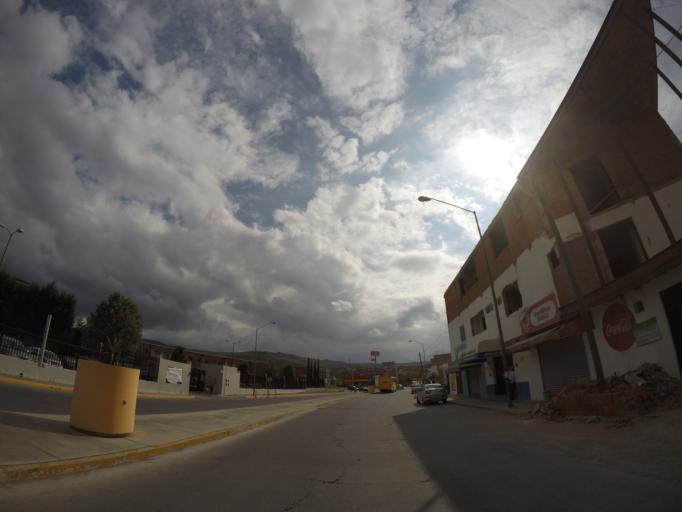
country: MX
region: San Luis Potosi
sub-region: San Luis Potosi
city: San Luis Potosi
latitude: 22.1242
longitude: -100.9851
